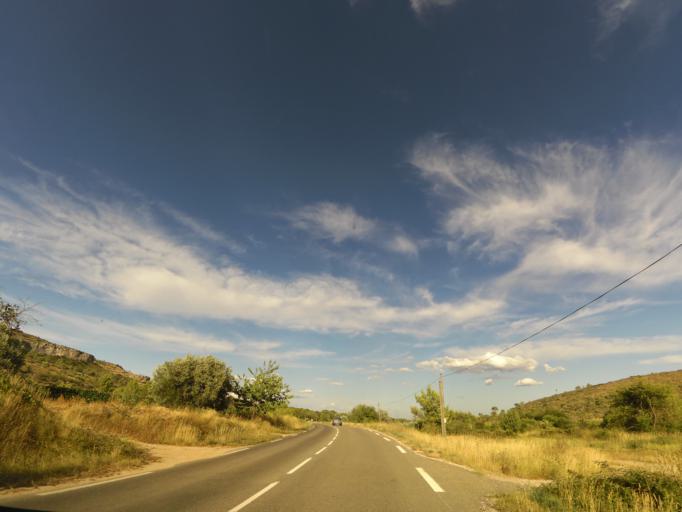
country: FR
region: Languedoc-Roussillon
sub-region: Departement de l'Herault
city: Saint-Drezery
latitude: 43.7696
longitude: 3.9402
